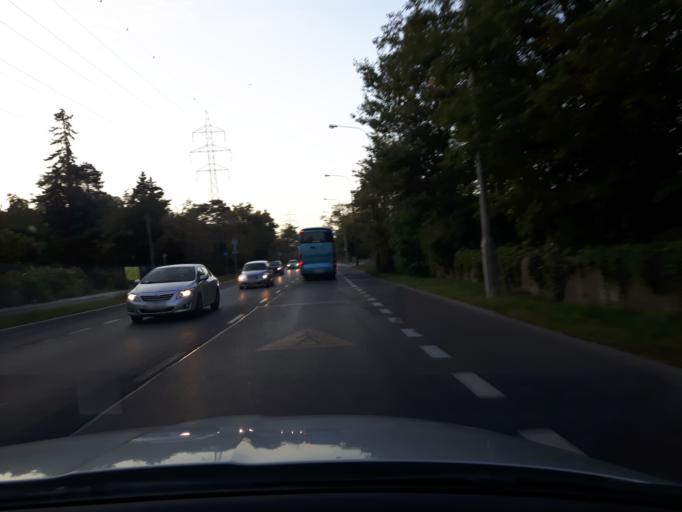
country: PL
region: Masovian Voivodeship
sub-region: Warszawa
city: Wawer
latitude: 52.2149
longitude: 21.1586
